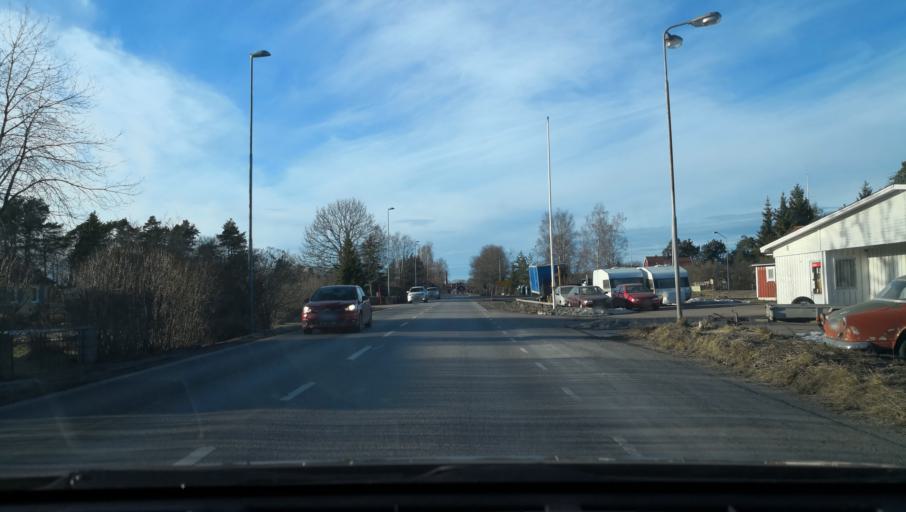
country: SE
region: Uppsala
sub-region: Osthammars Kommun
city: OEsthammar
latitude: 60.2835
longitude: 18.2925
